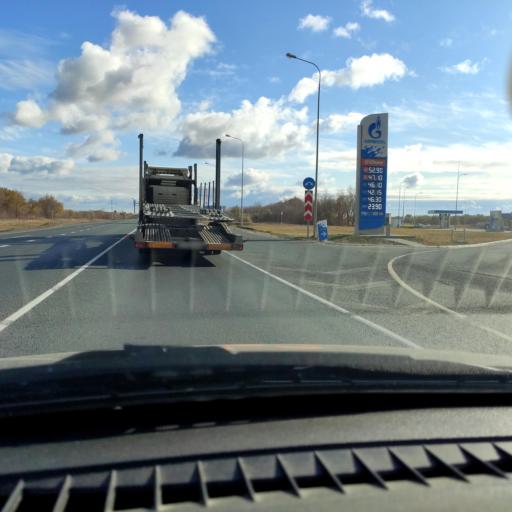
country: RU
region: Samara
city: Varlamovo
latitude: 53.1915
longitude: 48.3438
